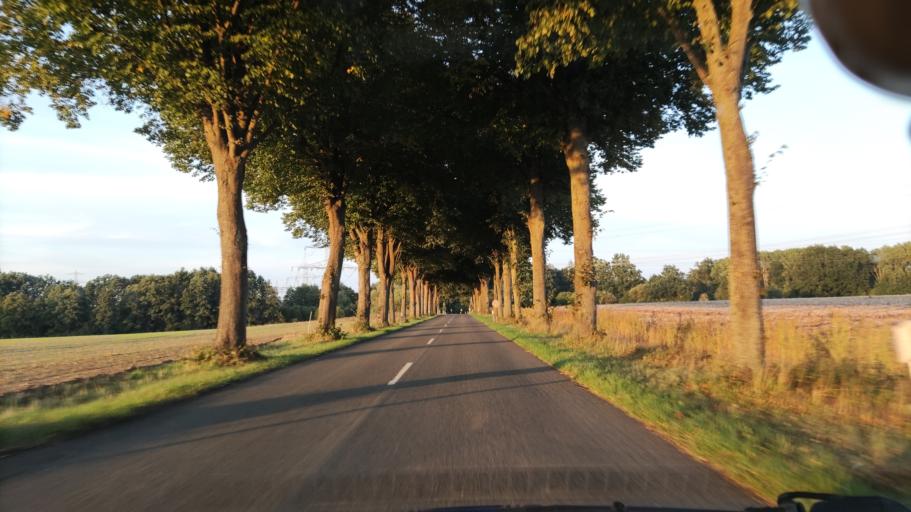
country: DE
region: Lower Saxony
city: Gerdau
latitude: 52.9869
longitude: 10.3769
